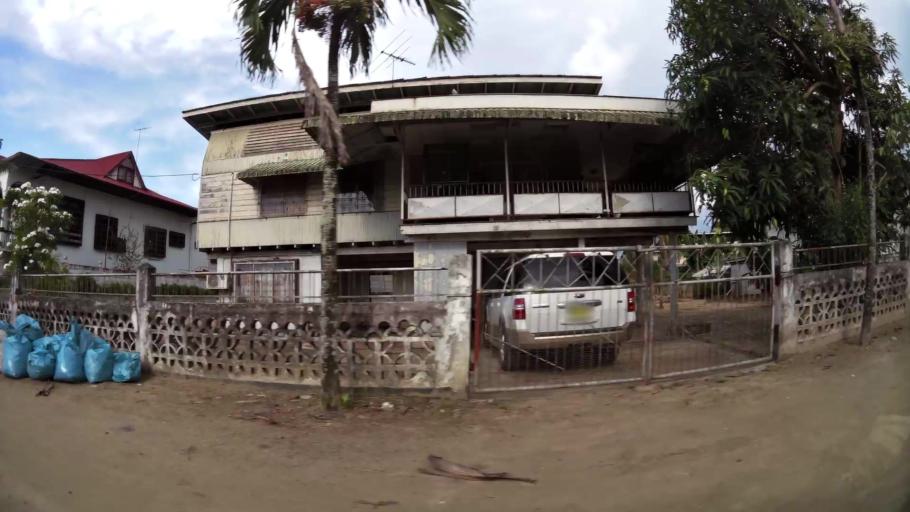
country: SR
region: Paramaribo
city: Paramaribo
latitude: 5.8422
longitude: -55.1844
